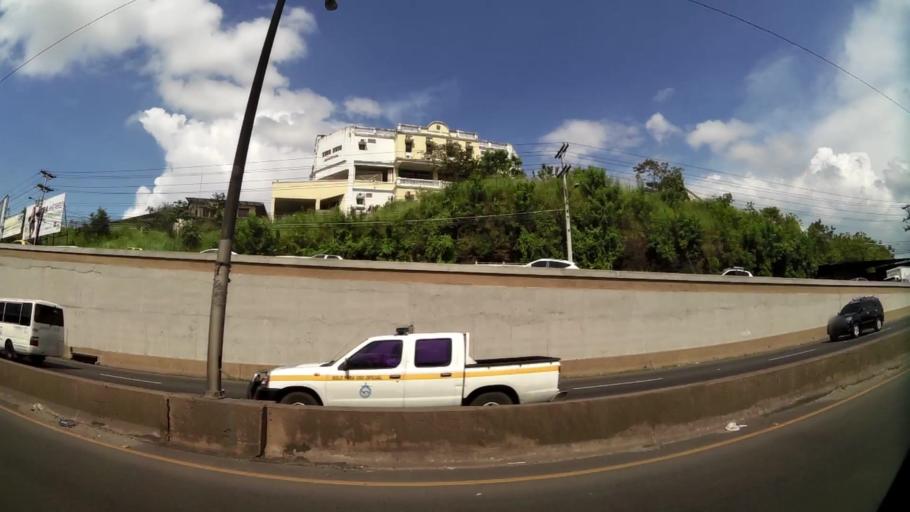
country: PA
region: Panama
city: San Miguelito
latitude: 9.0320
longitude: -79.4895
